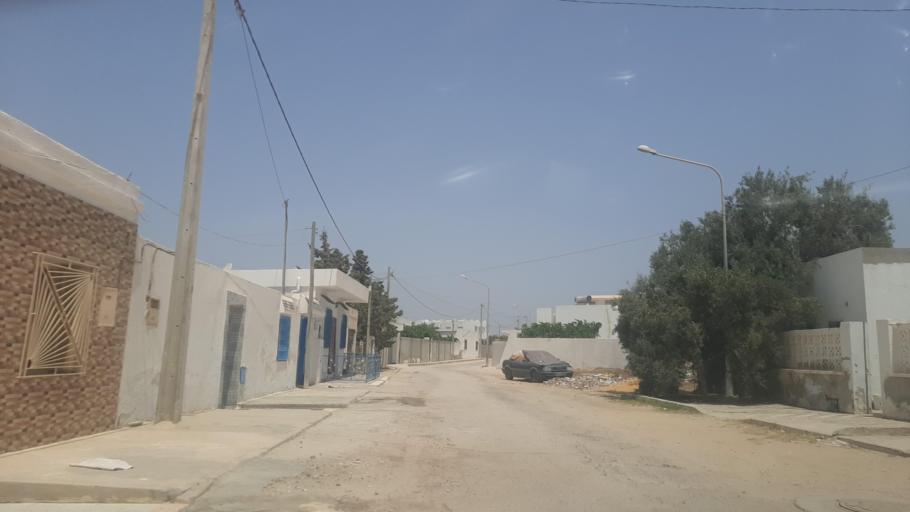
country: TN
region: Safaqis
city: Al Qarmadah
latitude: 34.7077
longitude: 11.2043
